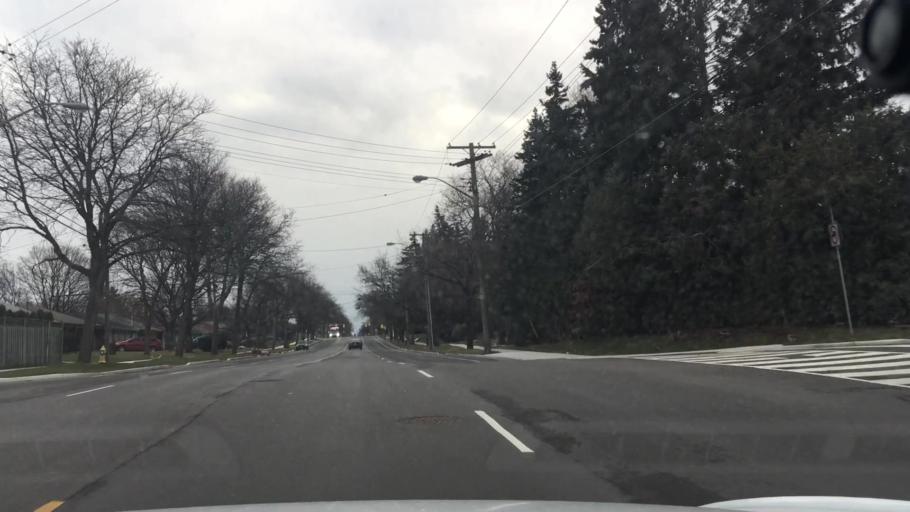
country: CA
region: Ontario
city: Scarborough
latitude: 43.7518
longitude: -79.2333
